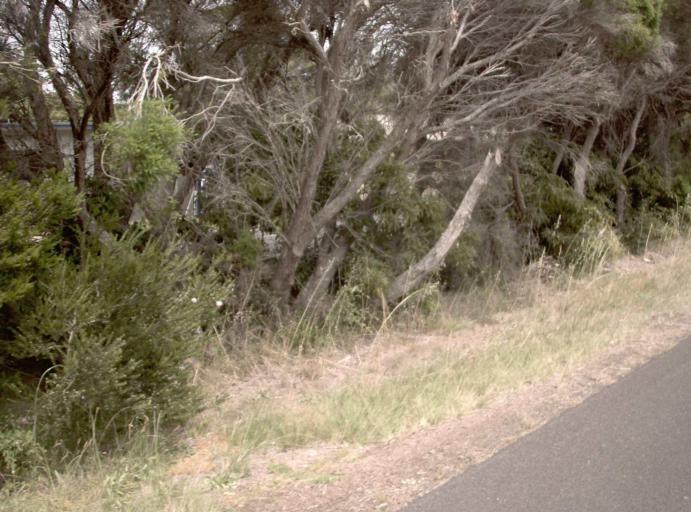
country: AU
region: Victoria
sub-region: Mornington Peninsula
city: Rosebud
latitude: -38.3645
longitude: 144.9172
